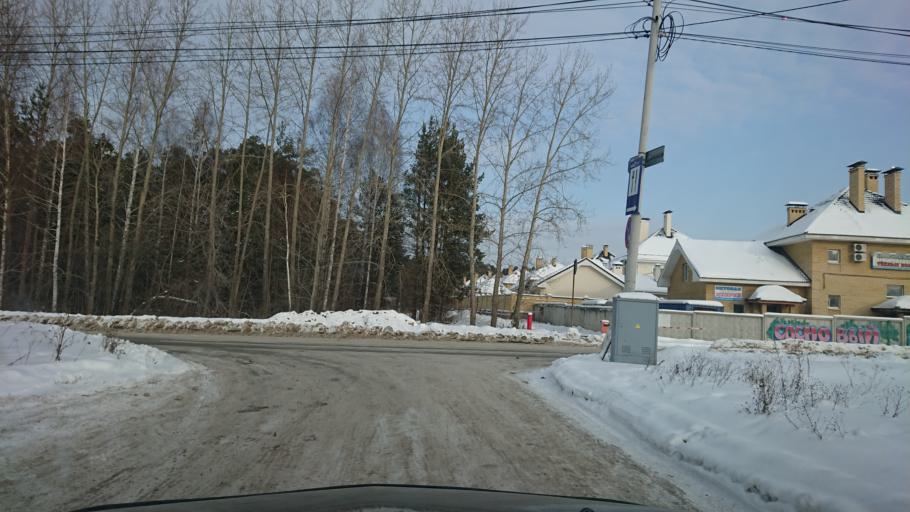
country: RU
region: Sverdlovsk
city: Sovkhoznyy
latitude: 56.7788
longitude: 60.5622
